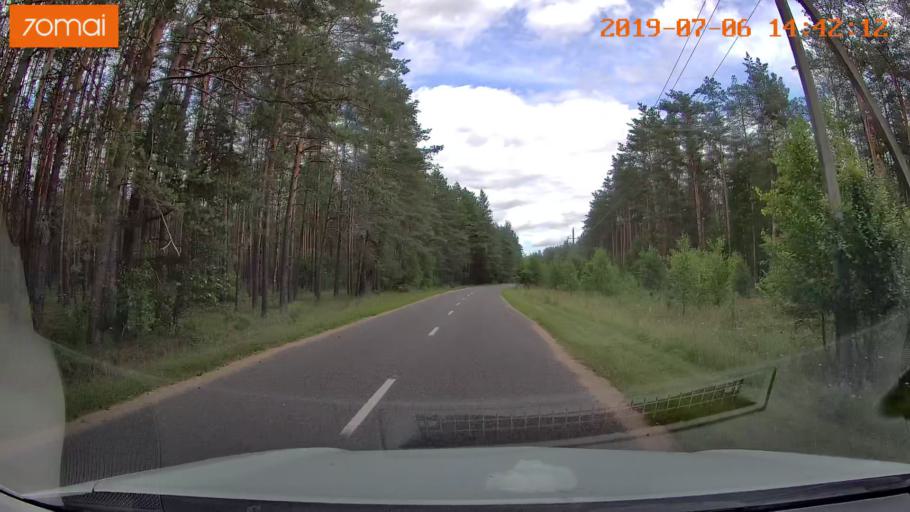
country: BY
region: Minsk
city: Ivyanyets
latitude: 53.9391
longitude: 26.6857
